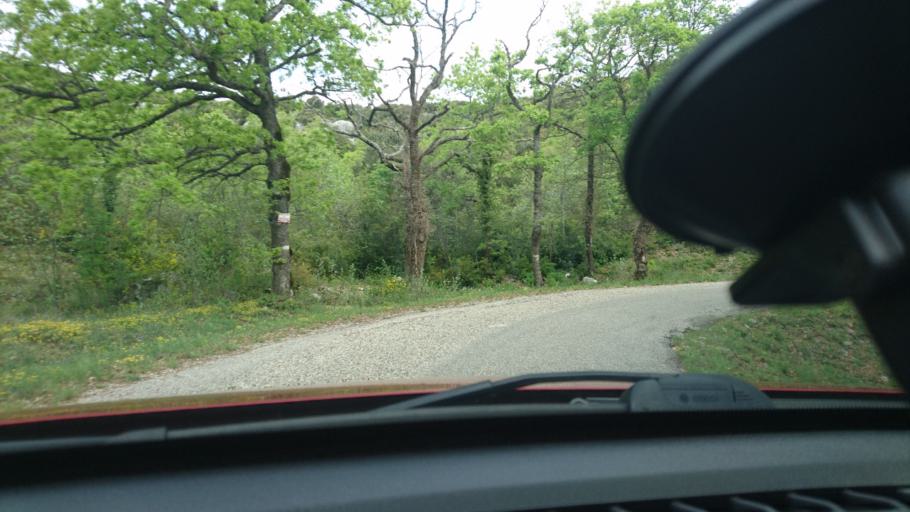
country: FR
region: Provence-Alpes-Cote d'Azur
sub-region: Departement du Vaucluse
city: Villes-sur-Auzon
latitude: 43.9926
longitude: 5.2847
